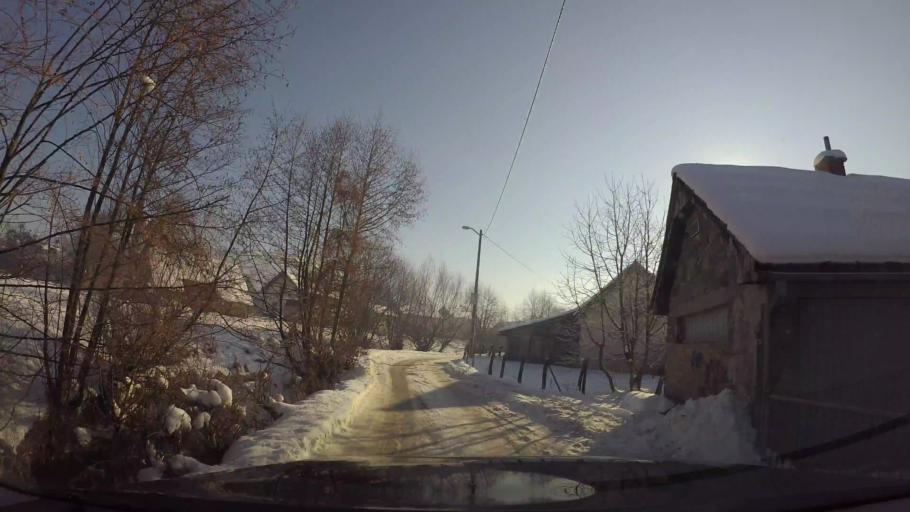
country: BA
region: Federation of Bosnia and Herzegovina
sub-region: Kanton Sarajevo
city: Sarajevo
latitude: 43.8212
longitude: 18.3756
